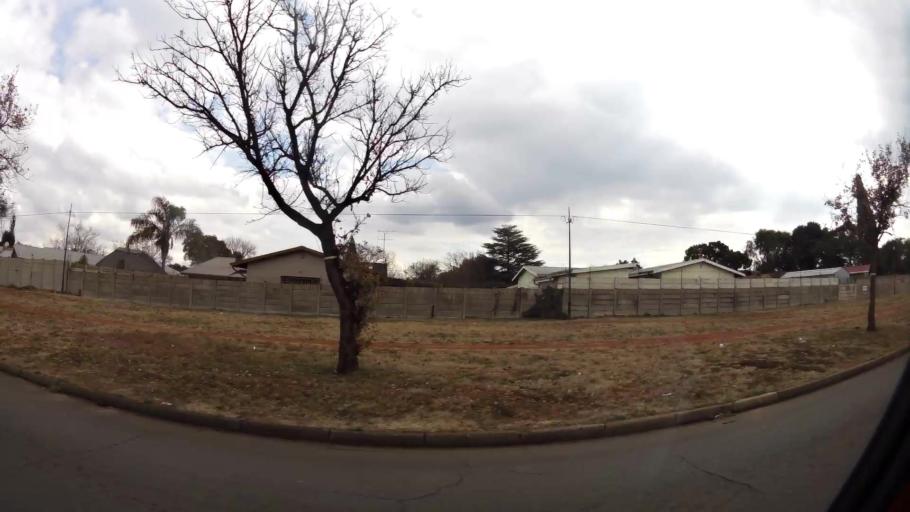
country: ZA
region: Gauteng
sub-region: Sedibeng District Municipality
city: Vanderbijlpark
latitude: -26.7245
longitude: 27.8370
